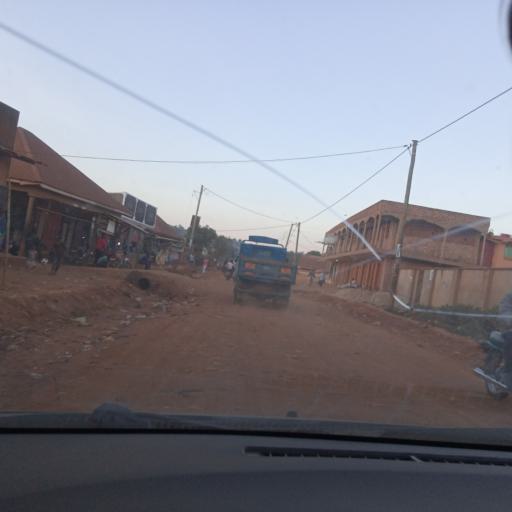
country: UG
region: Central Region
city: Masaka
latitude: -0.3218
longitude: 31.7638
